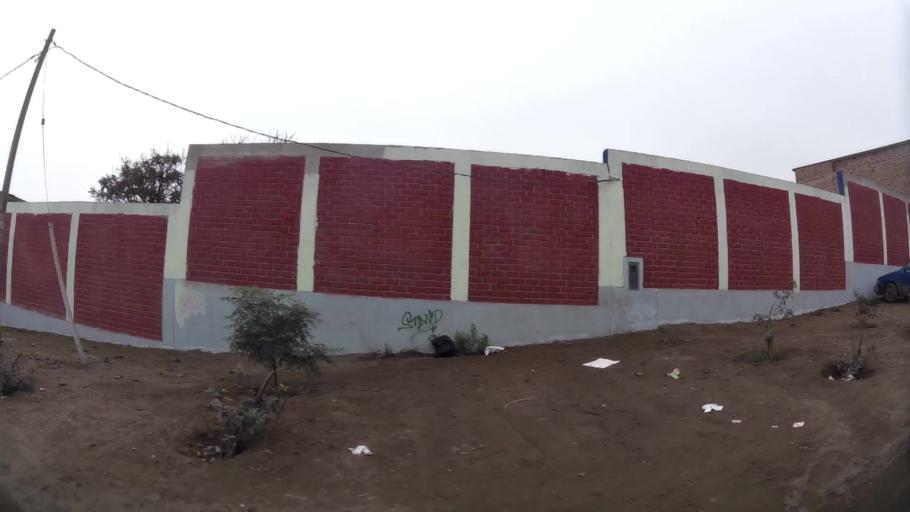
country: PE
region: Lima
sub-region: Lima
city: Surco
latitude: -12.1883
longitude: -76.9295
